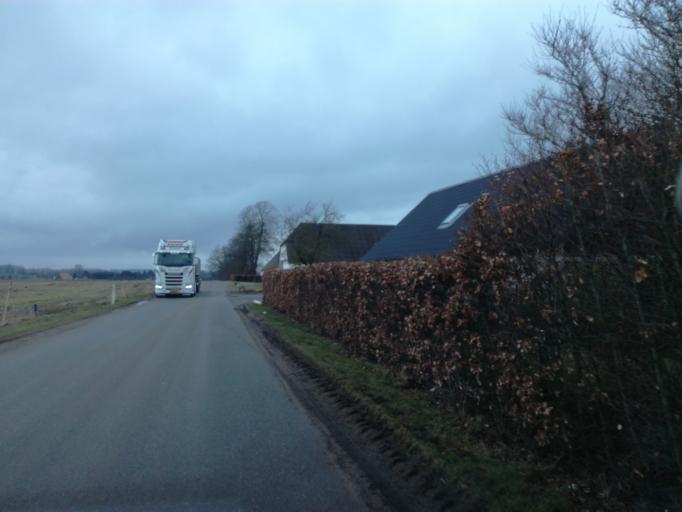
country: DK
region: South Denmark
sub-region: Vejle Kommune
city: Borkop
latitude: 55.5983
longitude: 9.6381
